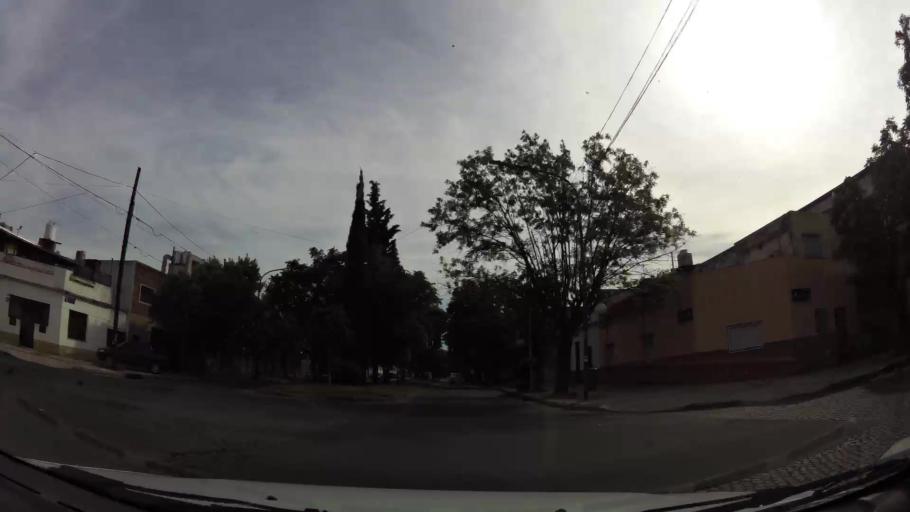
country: AR
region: Buenos Aires F.D.
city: Villa Lugano
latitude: -34.6543
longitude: -58.4915
